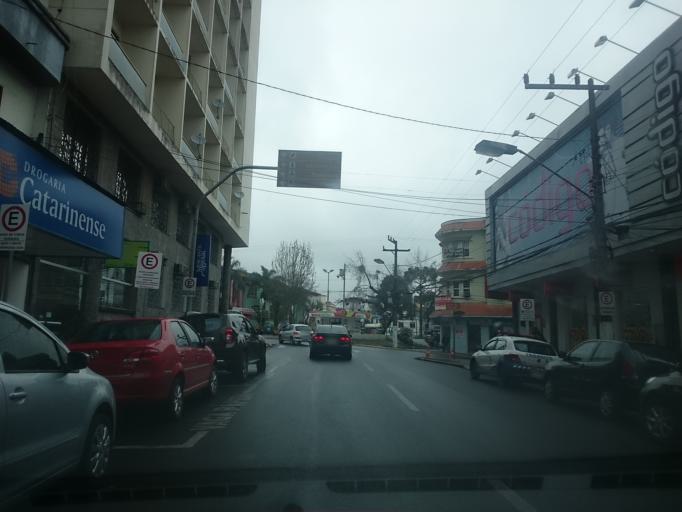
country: BR
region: Santa Catarina
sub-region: Lages
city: Lages
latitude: -27.8145
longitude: -50.3266
